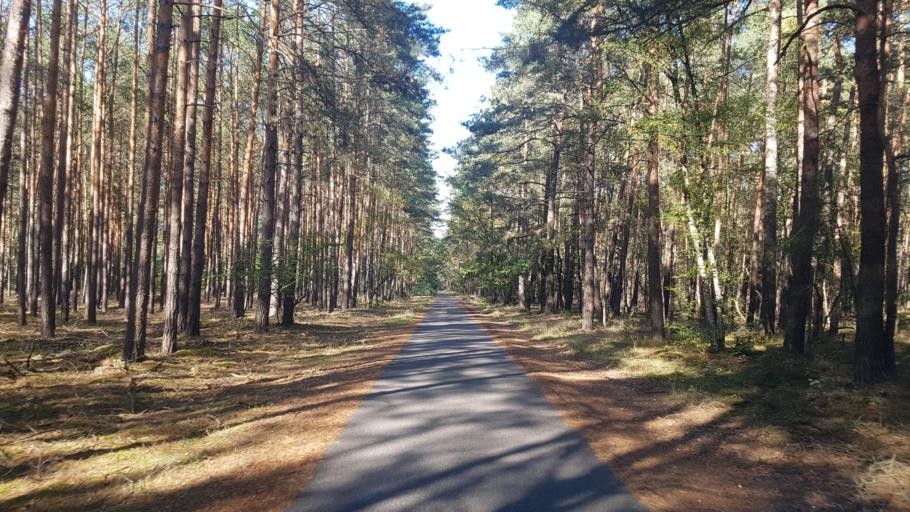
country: DE
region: Brandenburg
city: Ihlow
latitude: 51.8655
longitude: 13.2553
